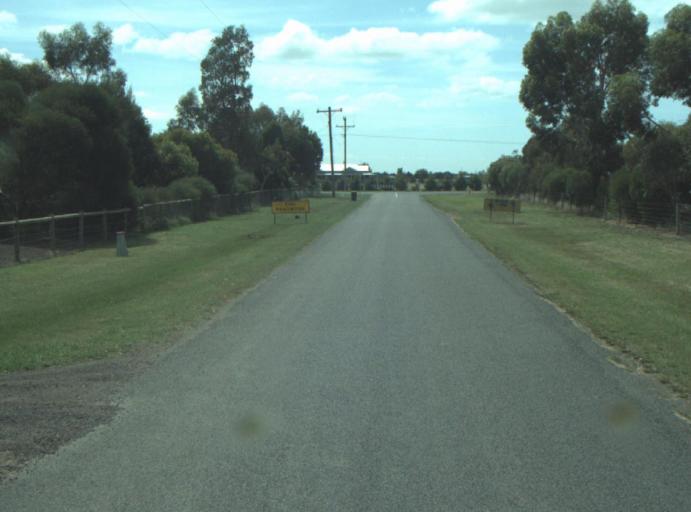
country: AU
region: Victoria
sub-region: Wyndham
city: Little River
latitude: -37.9657
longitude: 144.5057
